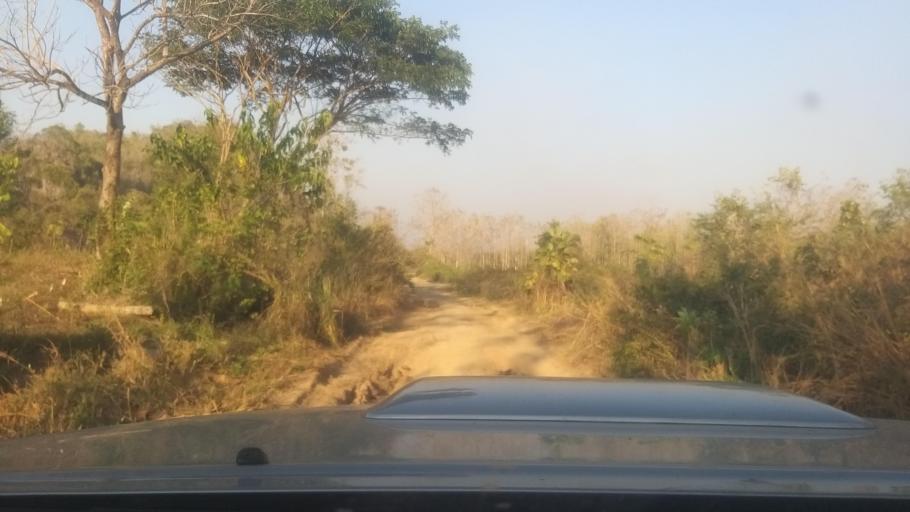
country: TH
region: Phrae
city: Nong Muang Khai
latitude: 18.2865
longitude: 100.0302
